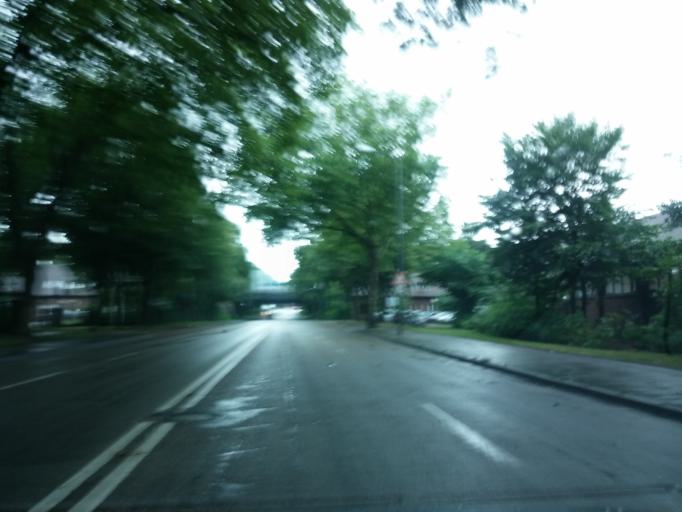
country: DE
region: North Rhine-Westphalia
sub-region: Regierungsbezirk Munster
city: Gelsenkirchen
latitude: 51.5619
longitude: 7.0723
